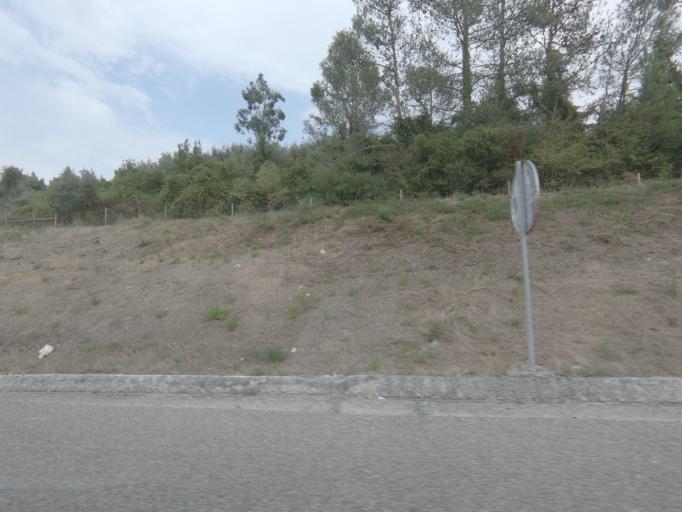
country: PT
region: Coimbra
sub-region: Coimbra
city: Coimbra
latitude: 40.2110
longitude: -8.4461
